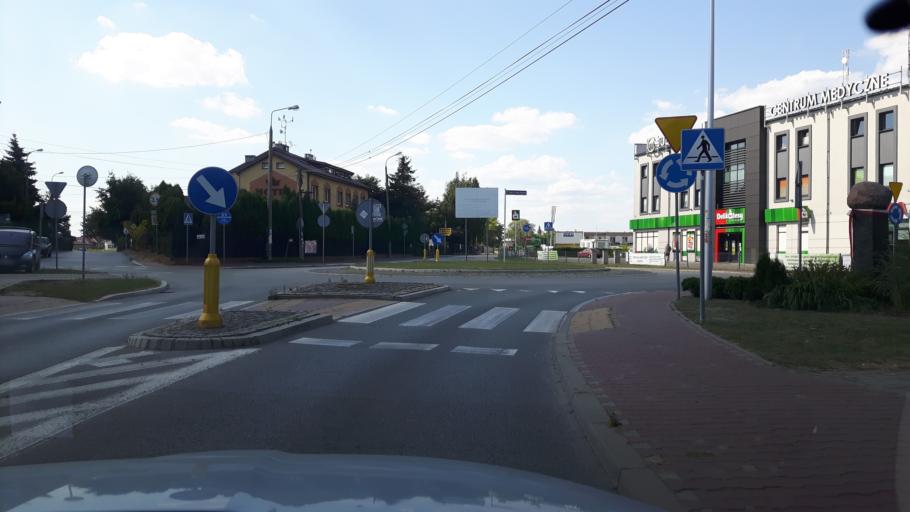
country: PL
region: Masovian Voivodeship
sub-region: Powiat pruszkowski
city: Nowe Grocholice
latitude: 52.1606
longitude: 20.9153
